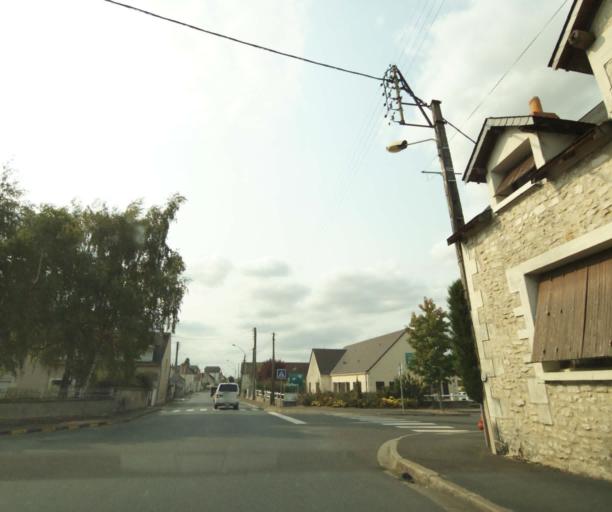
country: FR
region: Centre
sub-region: Departement de l'Indre
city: Chatillon-sur-Indre
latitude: 46.9901
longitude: 1.1704
